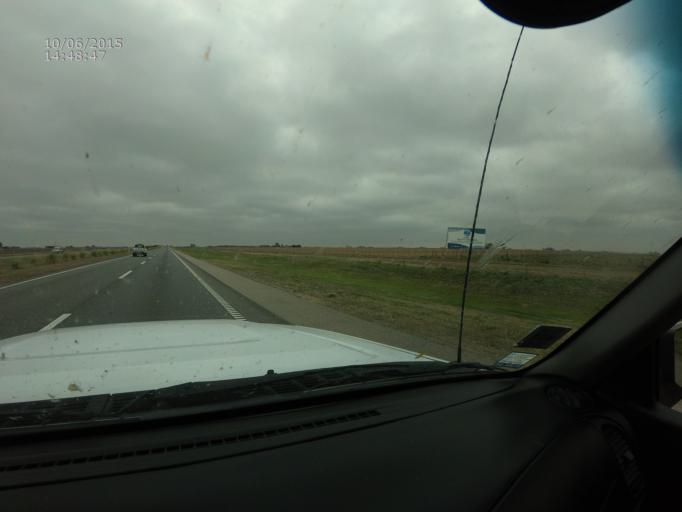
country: AR
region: Cordoba
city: Oncativo
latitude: -31.9382
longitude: -63.6093
